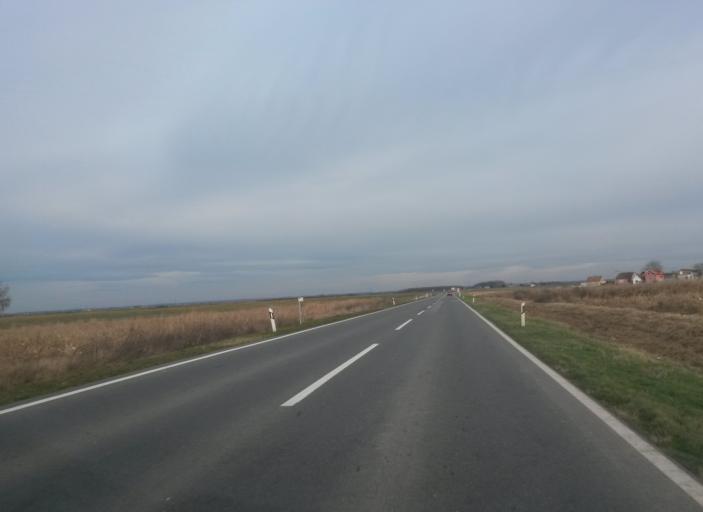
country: HR
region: Osjecko-Baranjska
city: Cepin
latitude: 45.5280
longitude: 18.5440
